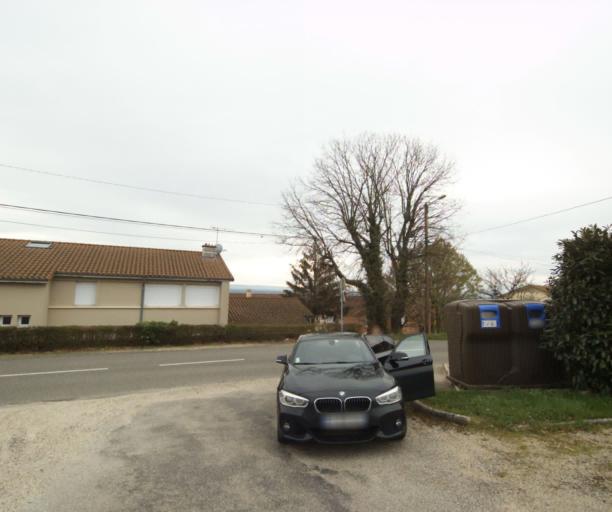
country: FR
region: Bourgogne
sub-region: Departement de Saone-et-Loire
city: Charnay-les-Macon
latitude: 46.3255
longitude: 4.7869
